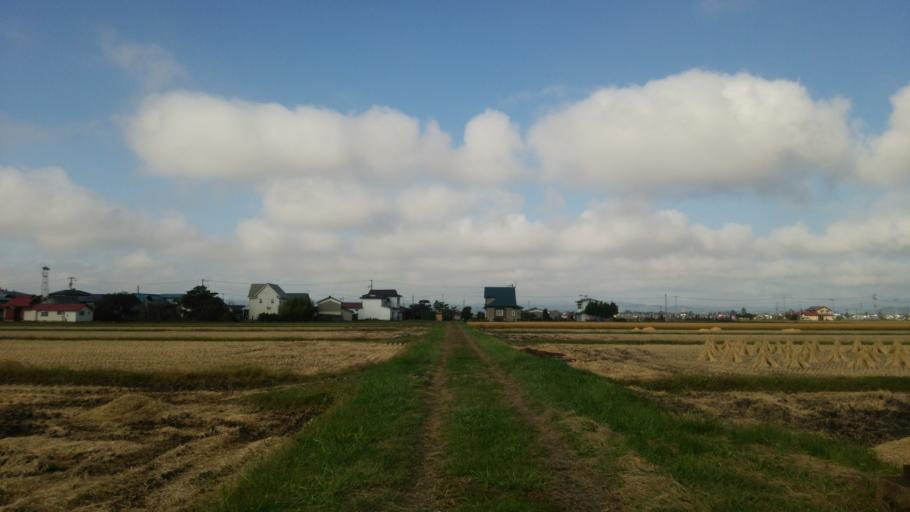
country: JP
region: Fukushima
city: Kitakata
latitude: 37.5658
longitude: 139.9108
